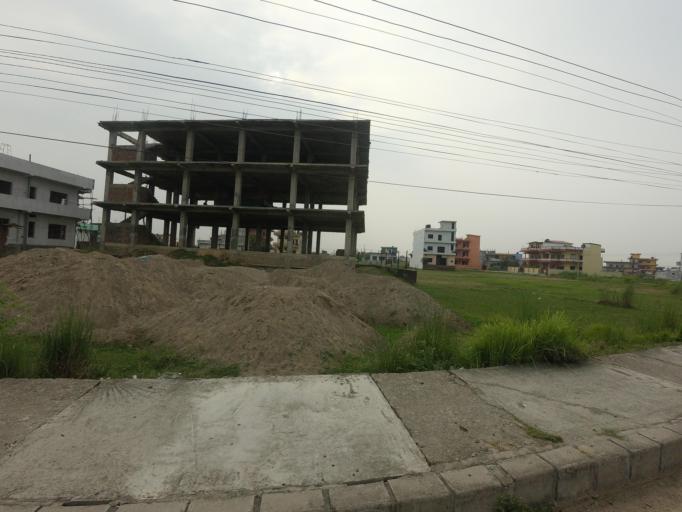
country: NP
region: Western Region
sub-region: Lumbini Zone
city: Bhairahawa
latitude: 27.4924
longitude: 83.4511
